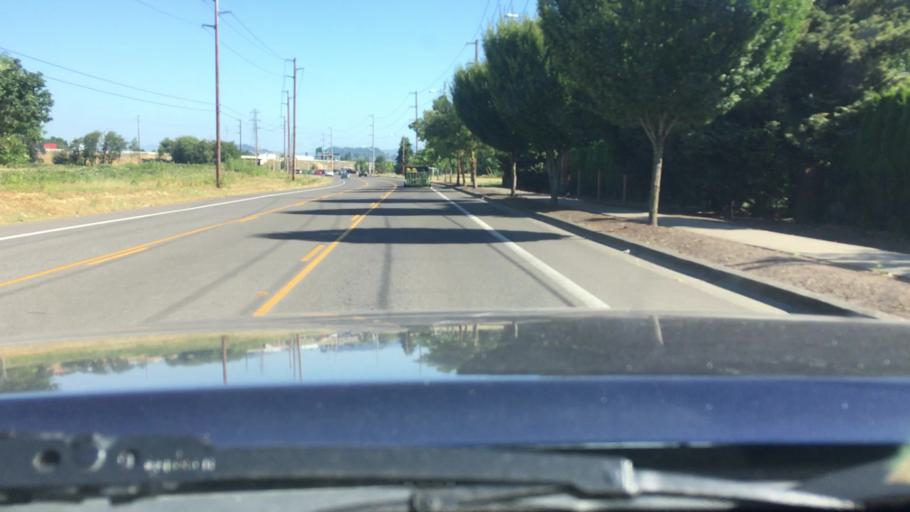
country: US
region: Oregon
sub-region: Lane County
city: Coburg
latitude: 44.0932
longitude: -123.0506
